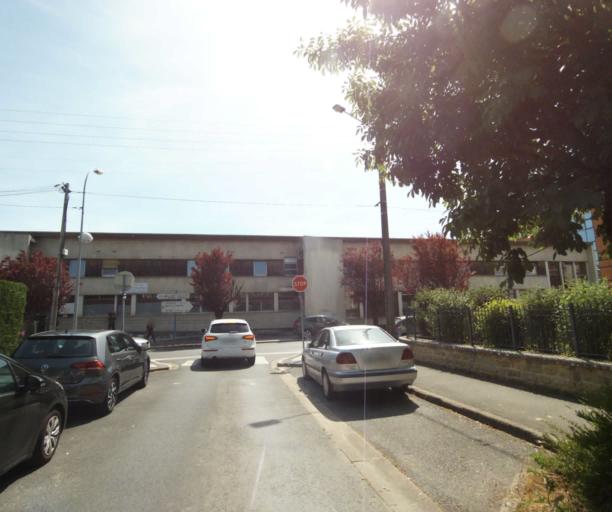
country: FR
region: Champagne-Ardenne
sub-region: Departement des Ardennes
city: Prix-les-Mezieres
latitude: 49.7629
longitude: 4.6991
